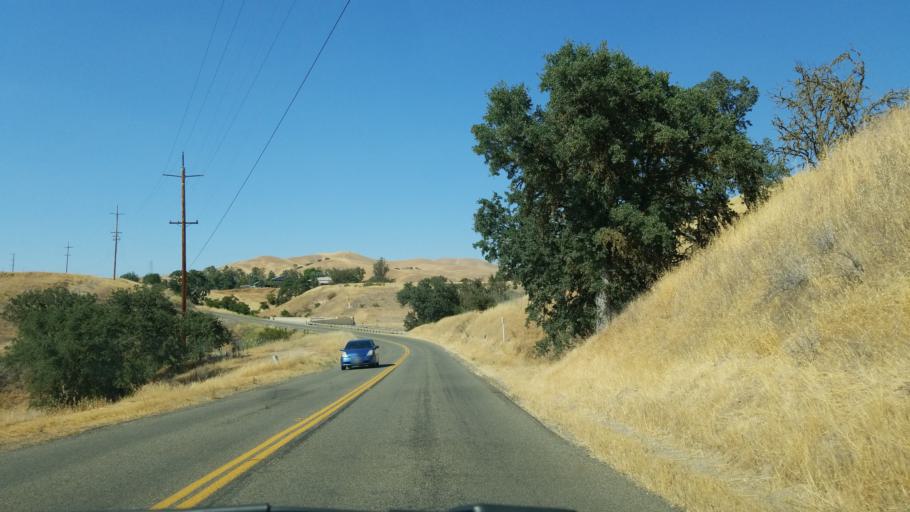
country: US
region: California
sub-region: San Luis Obispo County
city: San Miguel
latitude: 35.7489
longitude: -120.6832
